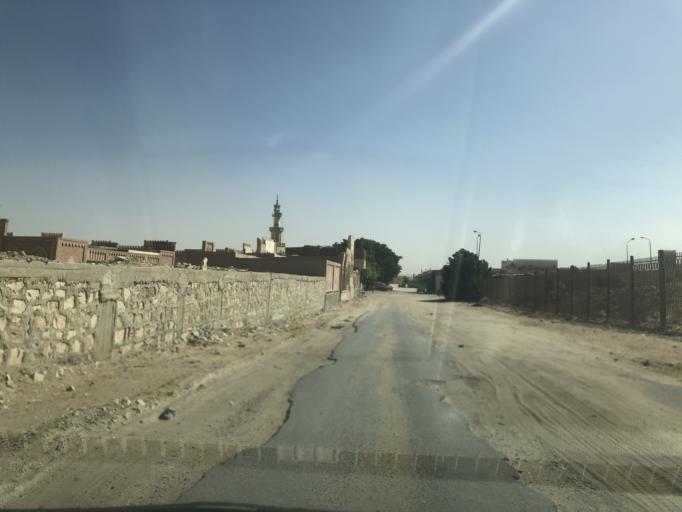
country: EG
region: Al Jizah
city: Madinat Sittah Uktubar
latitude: 29.9274
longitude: 30.9530
